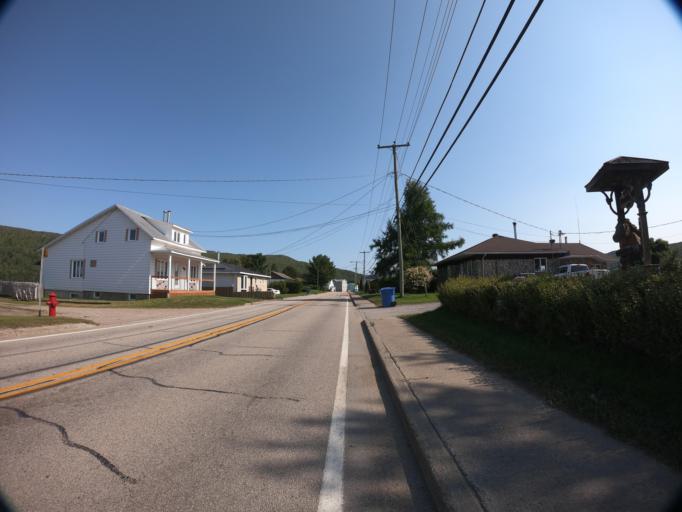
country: CA
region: Quebec
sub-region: Capitale-Nationale
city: Baie-Saint-Paul
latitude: 47.5531
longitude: -70.5332
